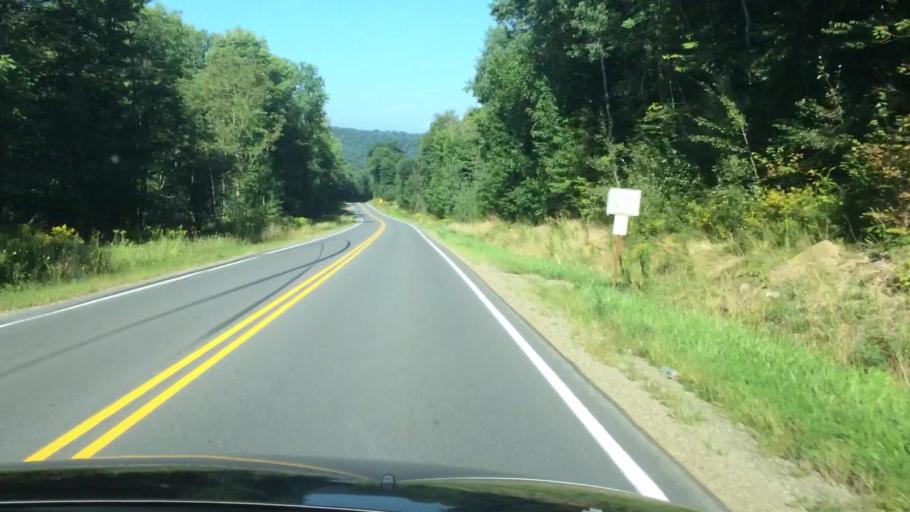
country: US
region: Pennsylvania
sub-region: McKean County
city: Bradford
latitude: 41.8842
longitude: -78.5821
